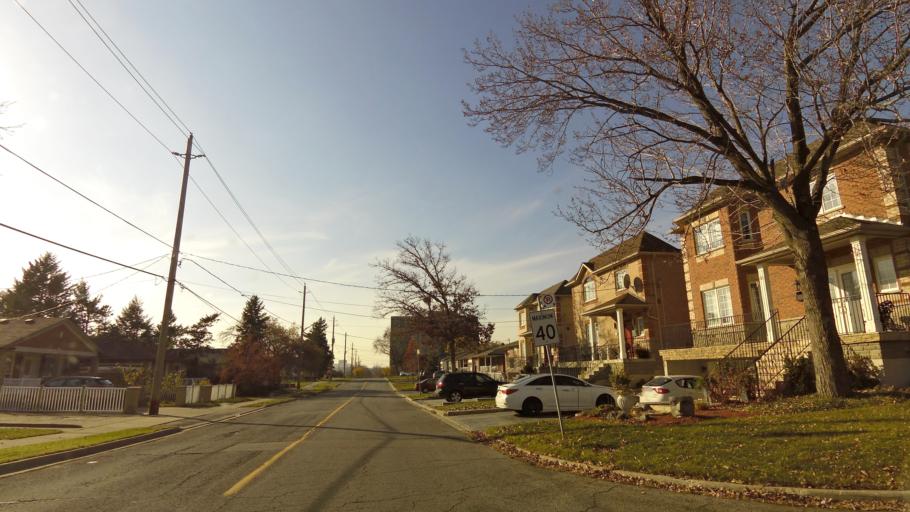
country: CA
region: Ontario
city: Concord
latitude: 43.7171
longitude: -79.4998
